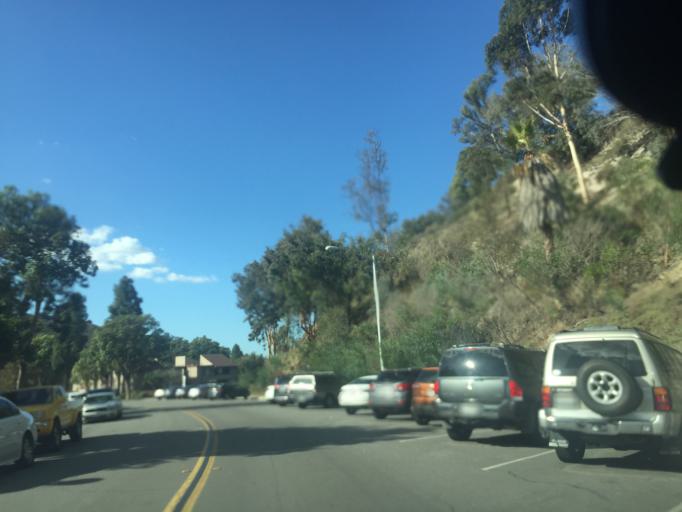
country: US
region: California
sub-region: San Diego County
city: La Mesa
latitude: 32.7823
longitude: -117.0795
